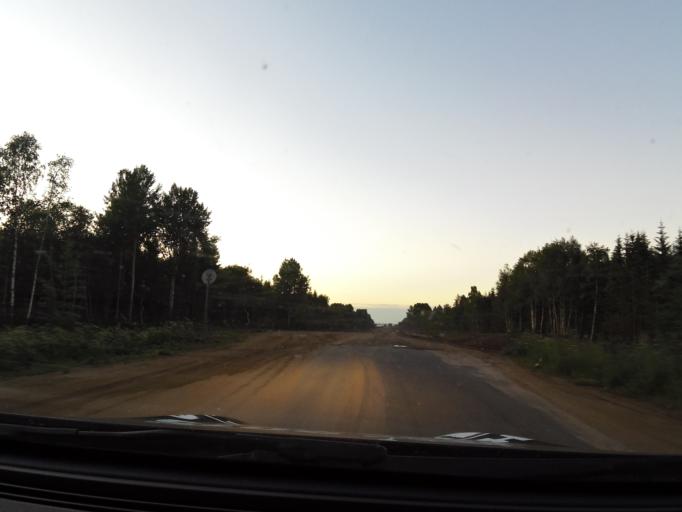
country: RU
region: Vologda
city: Vytegra
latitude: 60.9925
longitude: 36.1160
